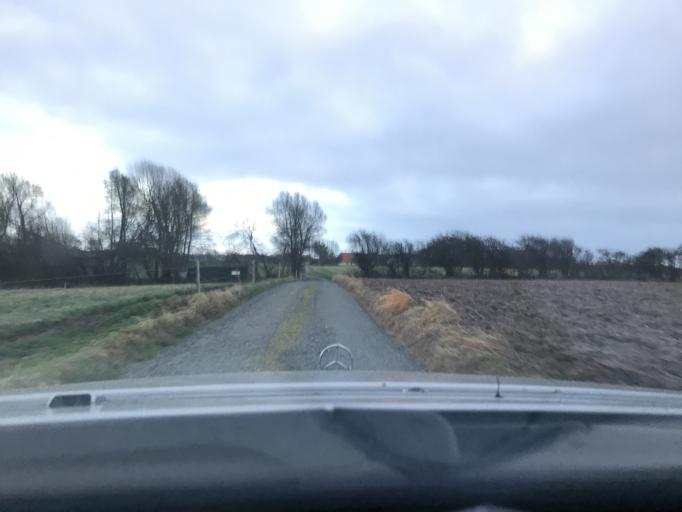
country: DK
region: South Denmark
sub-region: Sonderborg Kommune
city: Nordborg
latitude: 55.0711
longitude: 9.6909
